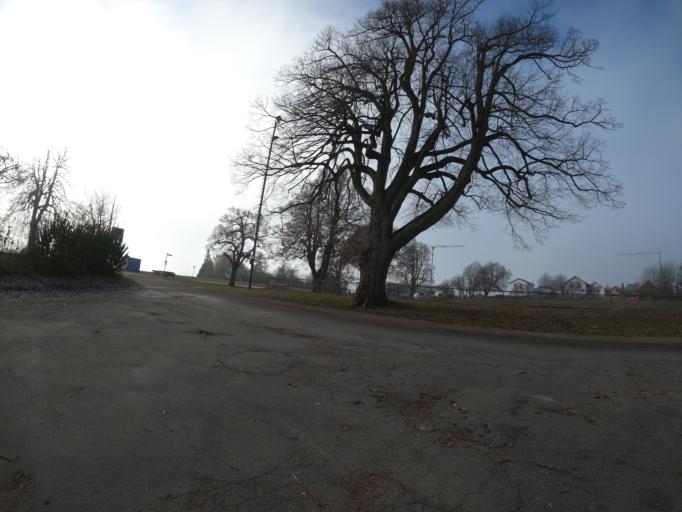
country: DE
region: Baden-Wuerttemberg
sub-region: Regierungsbezirk Stuttgart
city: Bad Uberkingen
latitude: 48.5848
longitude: 9.7711
